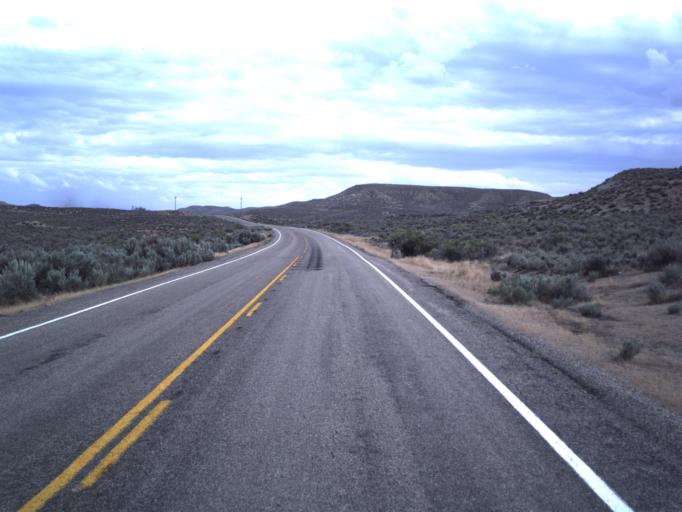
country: US
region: Colorado
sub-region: Rio Blanco County
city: Rangely
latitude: 40.0415
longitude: -109.1858
